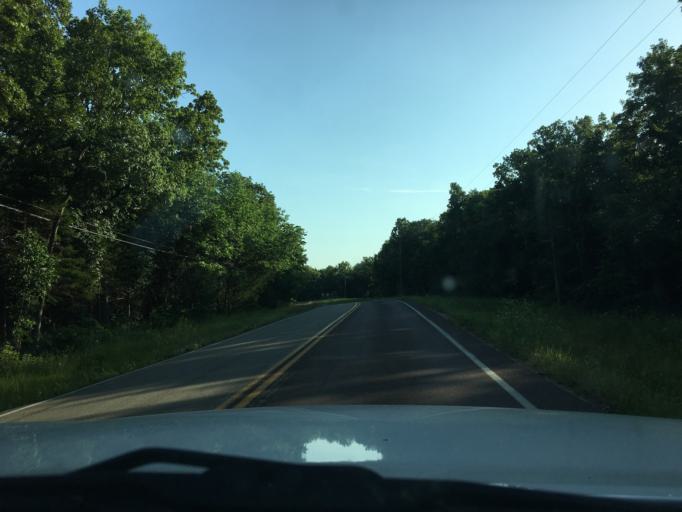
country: US
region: Missouri
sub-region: Gasconade County
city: Owensville
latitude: 38.4508
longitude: -91.6340
